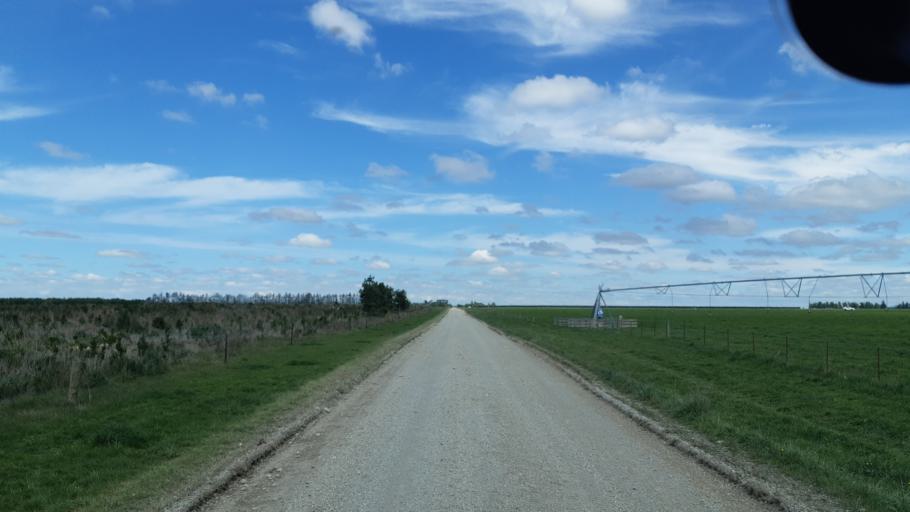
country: NZ
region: Canterbury
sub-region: Ashburton District
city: Methven
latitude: -43.7037
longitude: 171.4598
